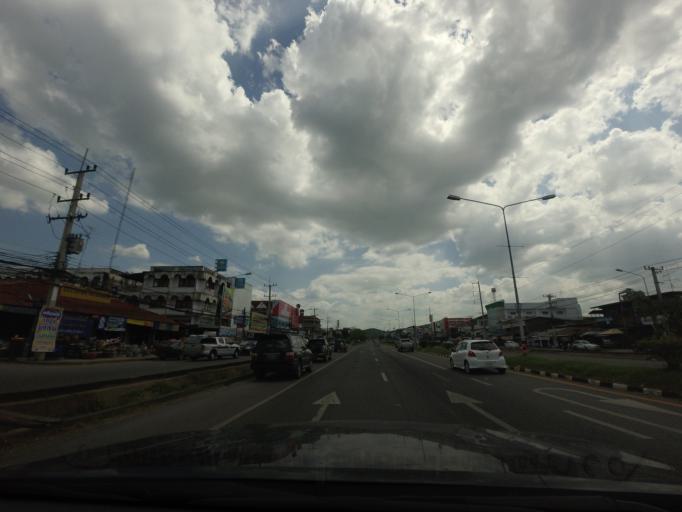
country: TH
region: Phetchabun
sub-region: Amphoe Bueng Sam Phan
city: Bueng Sam Phan
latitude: 15.7872
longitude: 101.0064
